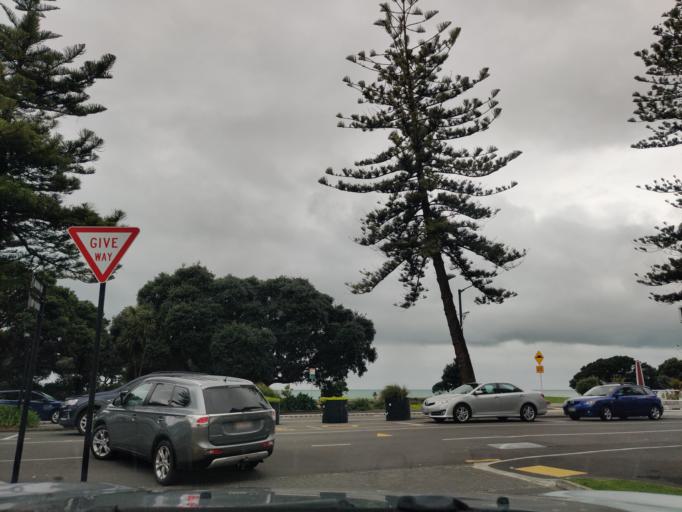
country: NZ
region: Hawke's Bay
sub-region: Napier City
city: Napier
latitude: -39.4919
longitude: 176.9189
